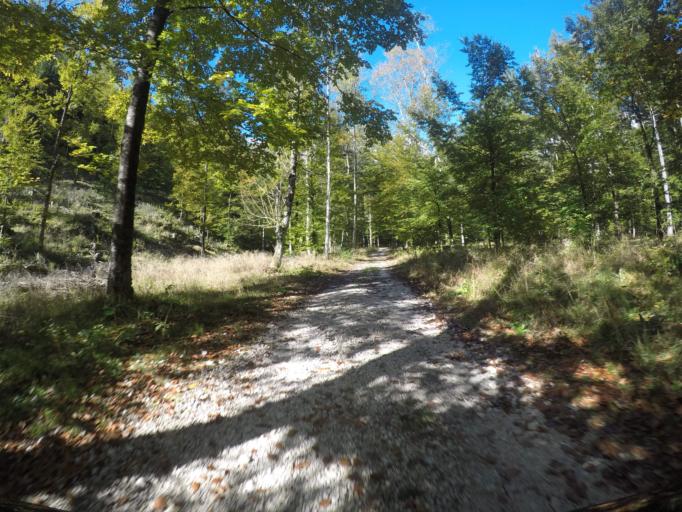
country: SI
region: Kamnik
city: Mekinje
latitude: 46.3275
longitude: 14.5842
